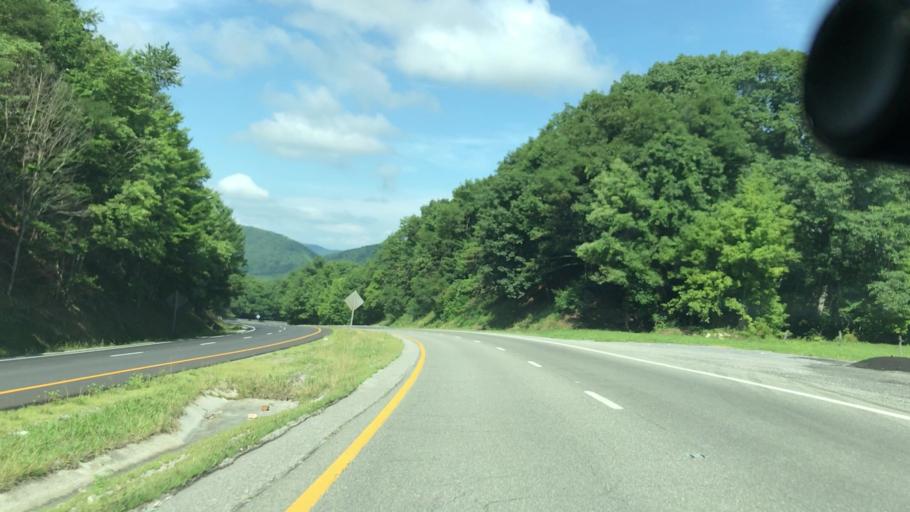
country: US
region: Virginia
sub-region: Montgomery County
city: Blacksburg
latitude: 37.2826
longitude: -80.4450
